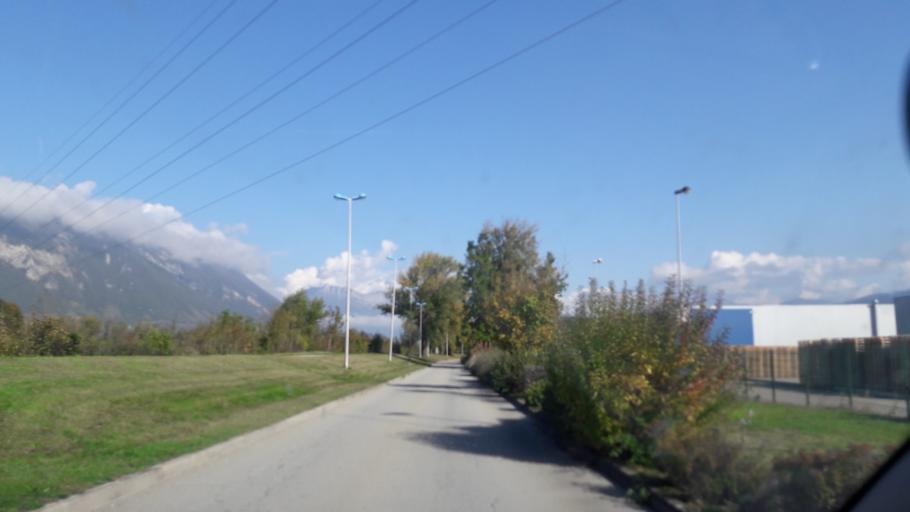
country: FR
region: Rhone-Alpes
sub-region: Departement de la Savoie
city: Les Marches
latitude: 45.4769
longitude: 6.0258
